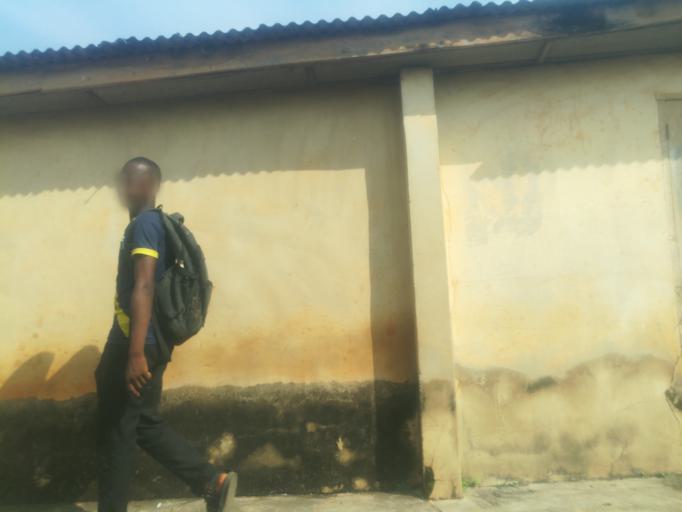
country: NG
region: Oyo
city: Ibadan
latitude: 7.3920
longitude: 3.8210
